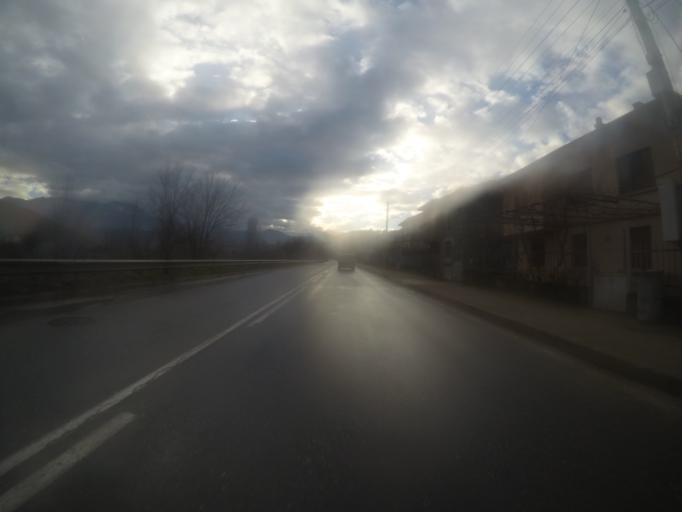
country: BG
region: Blagoevgrad
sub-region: Obshtina Simitli
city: Simitli
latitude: 41.8834
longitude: 23.1209
